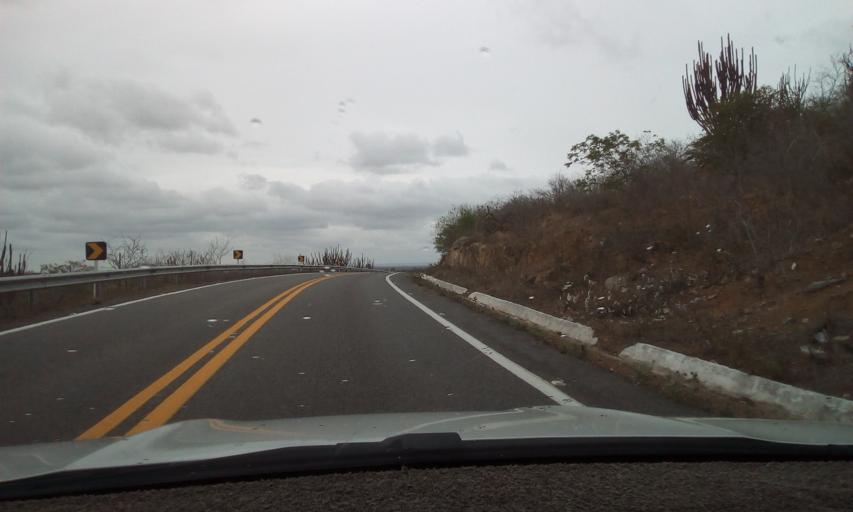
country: BR
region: Paraiba
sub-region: Areia
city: Remigio
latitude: -6.8862
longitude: -35.9211
